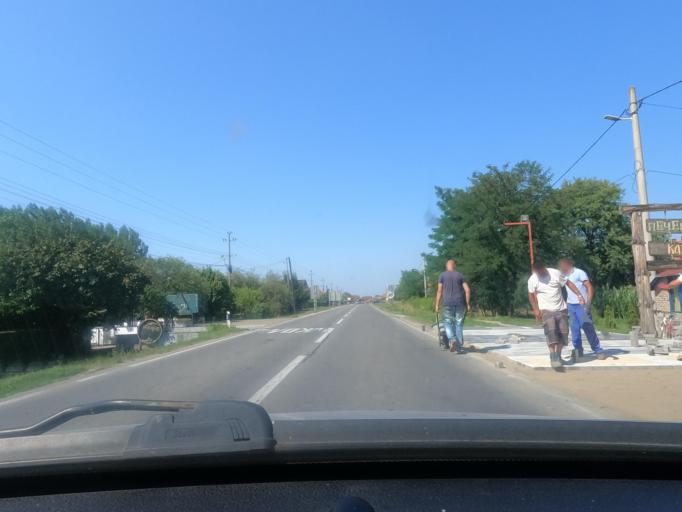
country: RS
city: Lipnicki Sor
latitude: 44.5843
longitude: 19.2561
